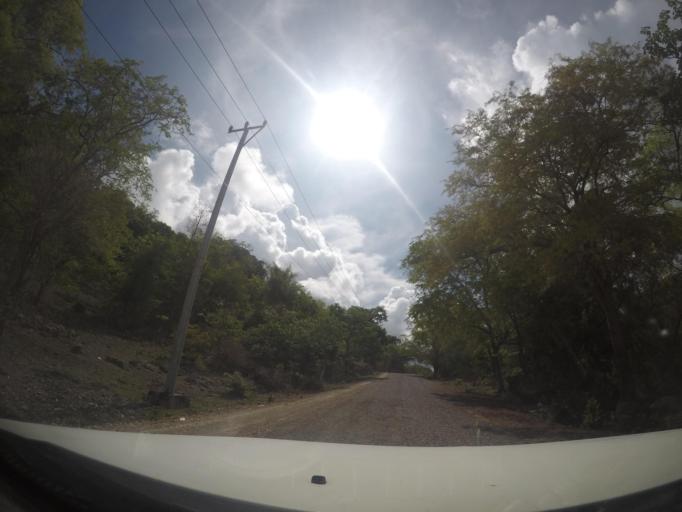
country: TL
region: Lautem
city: Lospalos
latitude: -8.3439
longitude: 127.0338
